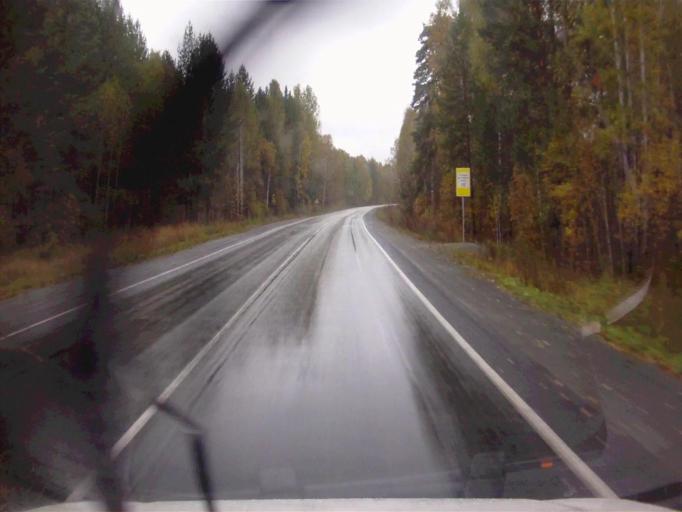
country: RU
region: Chelyabinsk
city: Tayginka
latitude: 55.5960
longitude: 60.6193
